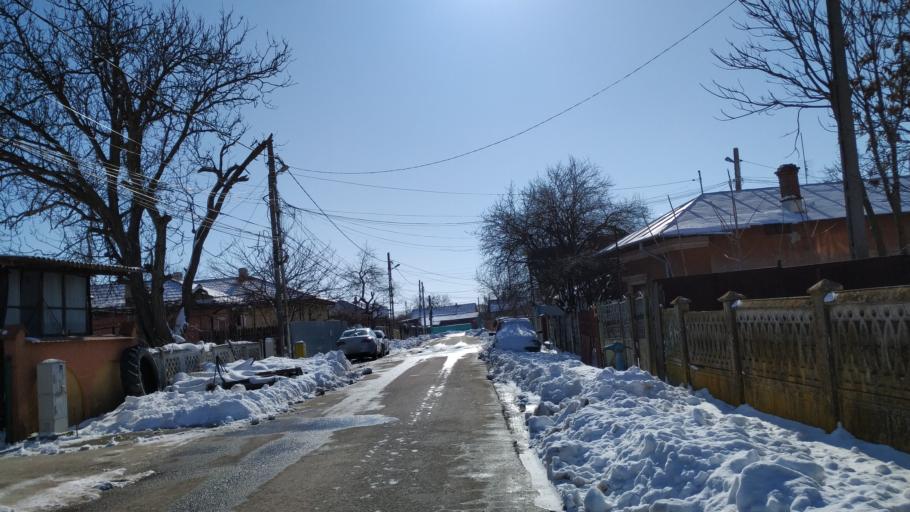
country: RO
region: Ilfov
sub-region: Comuna Berceni
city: Berceni
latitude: 44.3179
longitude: 26.1856
